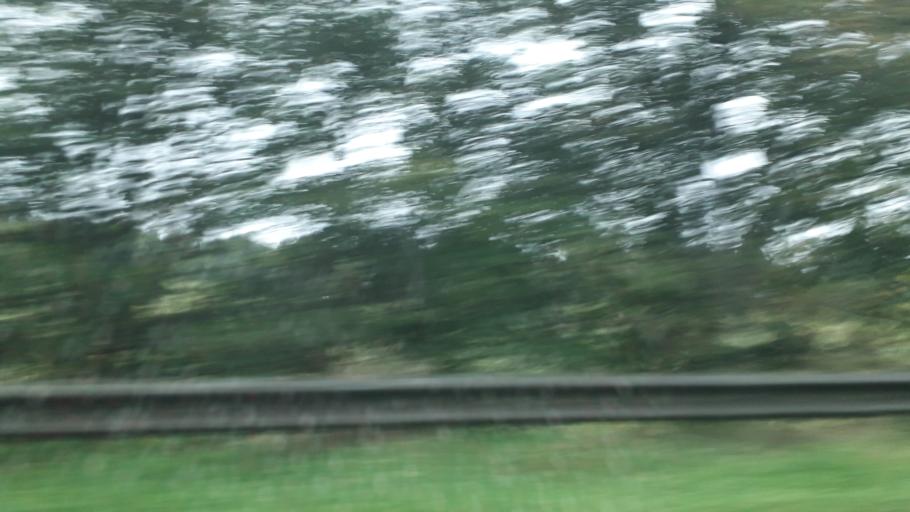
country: IE
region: Leinster
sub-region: An Iarmhi
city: An Muileann gCearr
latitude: 53.6097
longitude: -7.4386
